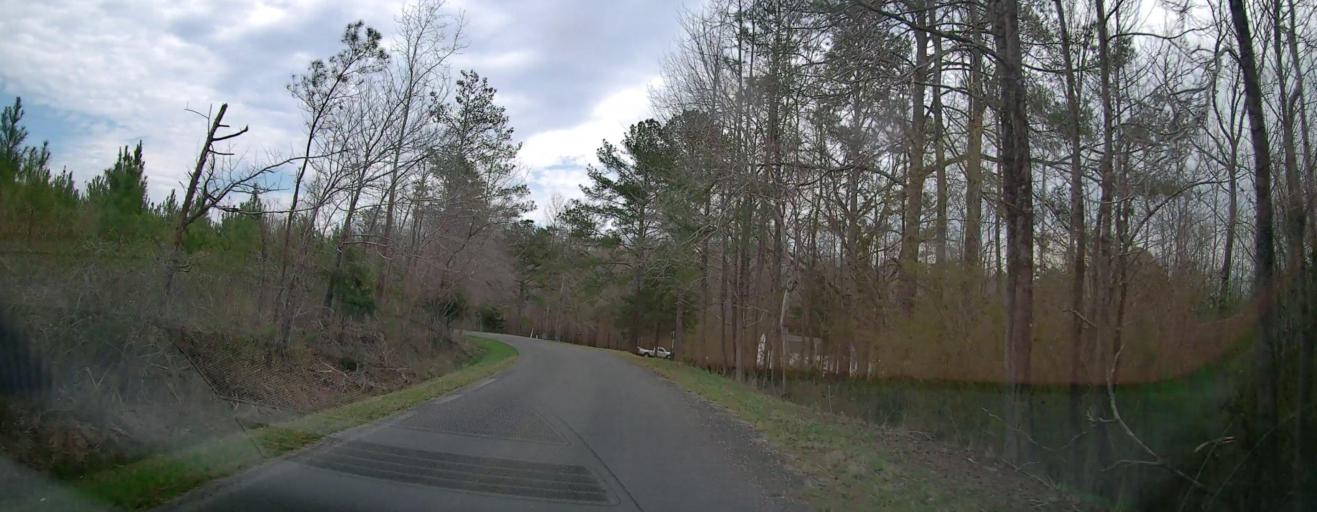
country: US
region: Alabama
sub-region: Marion County
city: Hamilton
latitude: 34.1996
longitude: -88.1862
